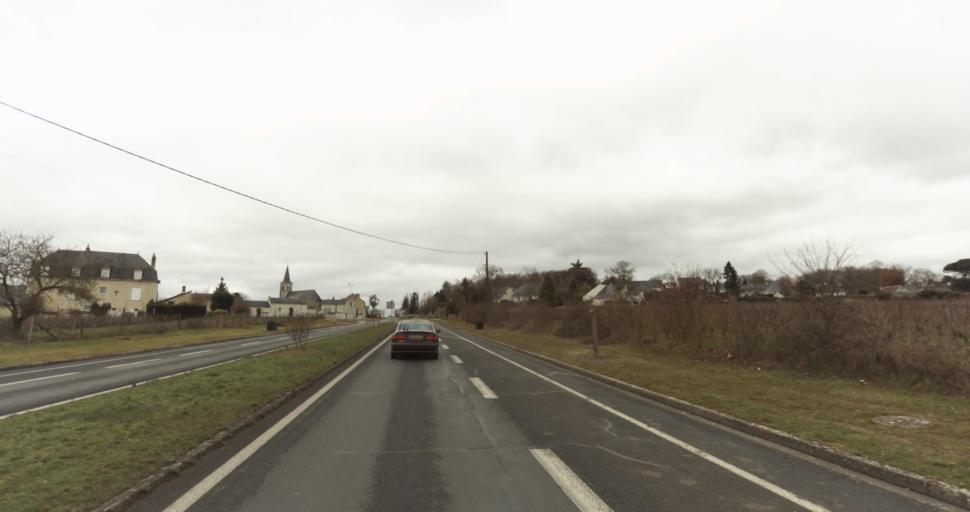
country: FR
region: Pays de la Loire
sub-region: Departement de Maine-et-Loire
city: Varrains
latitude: 47.2247
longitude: -0.0642
